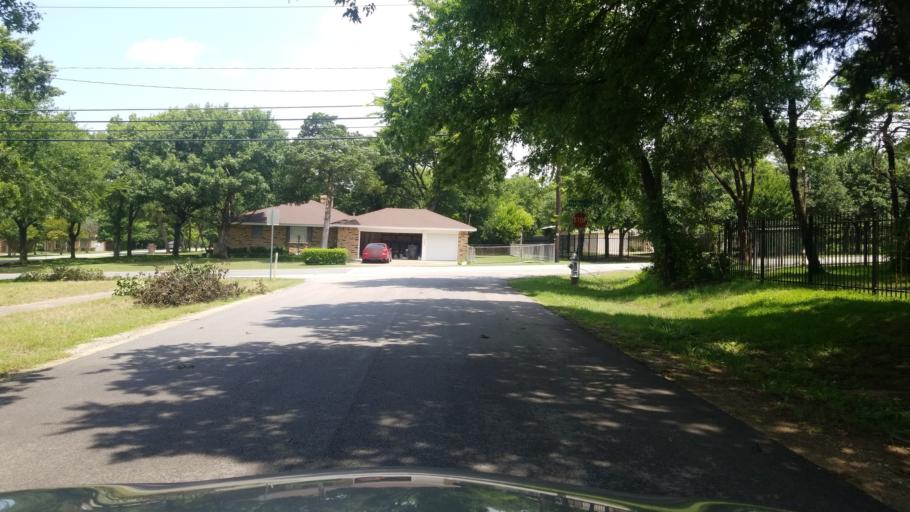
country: US
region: Texas
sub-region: Dallas County
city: Duncanville
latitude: 32.6798
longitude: -96.9215
